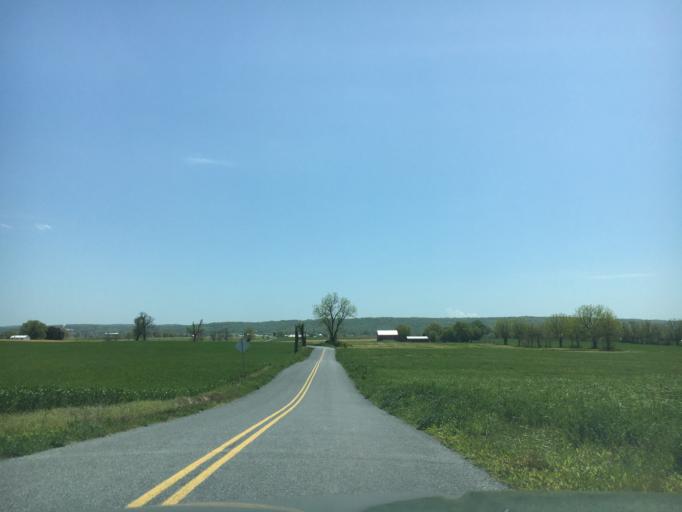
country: US
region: Pennsylvania
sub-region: Berks County
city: Fleetwood
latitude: 40.4847
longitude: -75.8314
